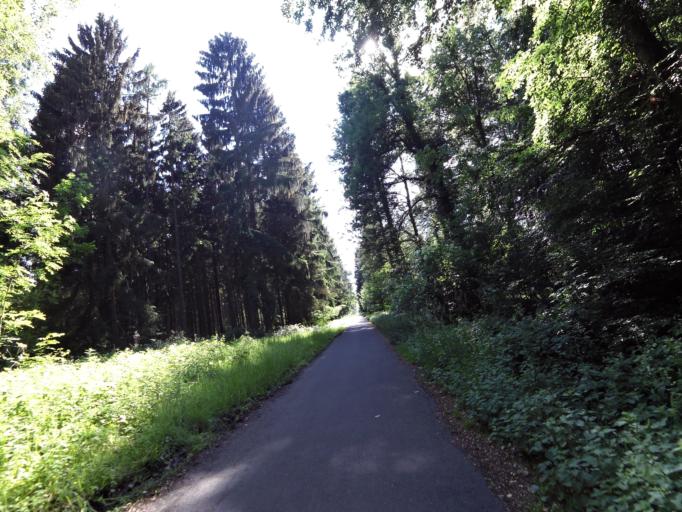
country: DE
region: North Rhine-Westphalia
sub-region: Regierungsbezirk Koln
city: Wachtberg
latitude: 50.6760
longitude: 7.1053
